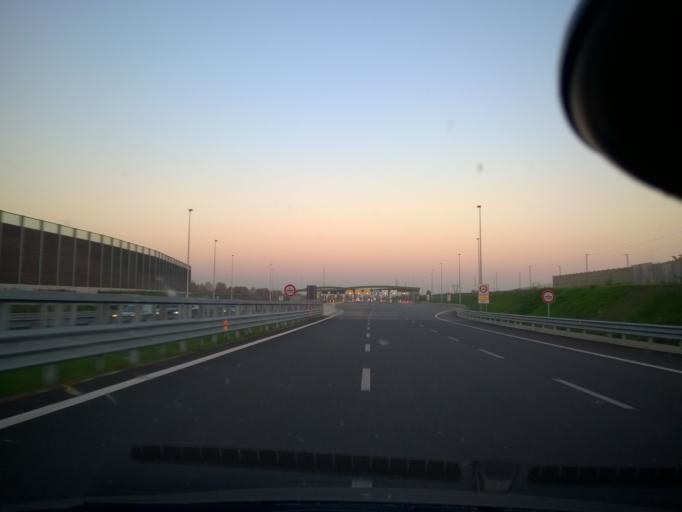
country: IT
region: Lombardy
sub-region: Provincia di Brescia
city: Castelcovati
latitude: 45.5217
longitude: 9.9583
